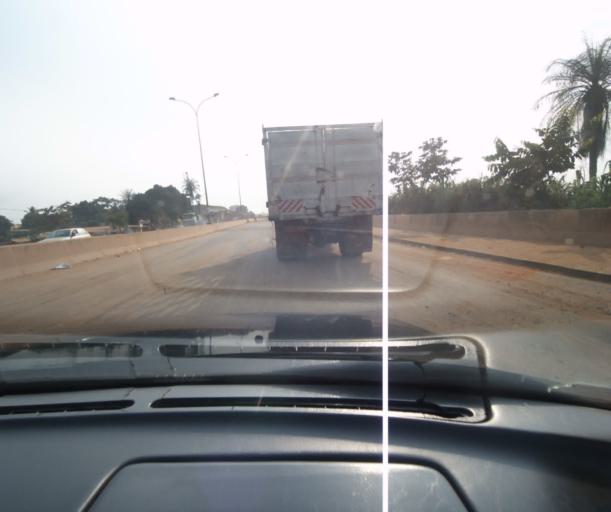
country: CM
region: Centre
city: Okoa
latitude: 3.9544
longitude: 11.5309
